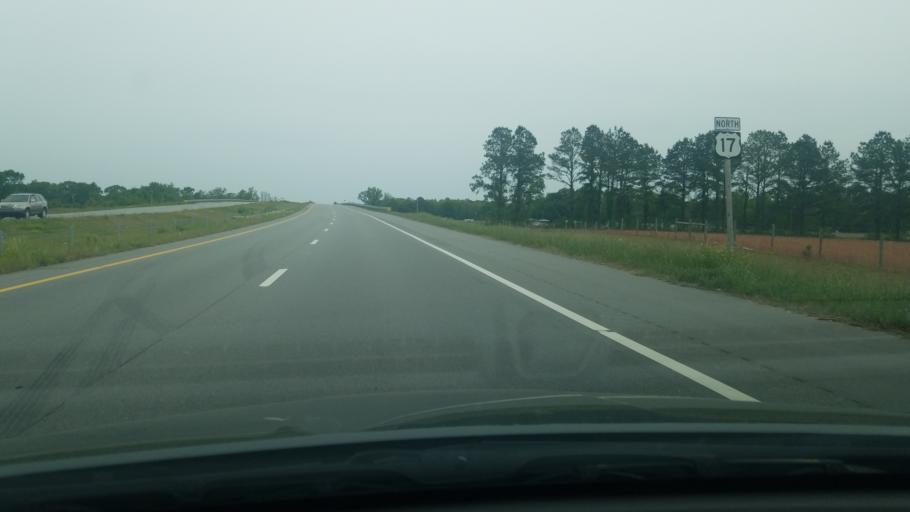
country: US
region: North Carolina
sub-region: Jones County
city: Maysville
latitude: 35.0074
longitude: -77.2292
